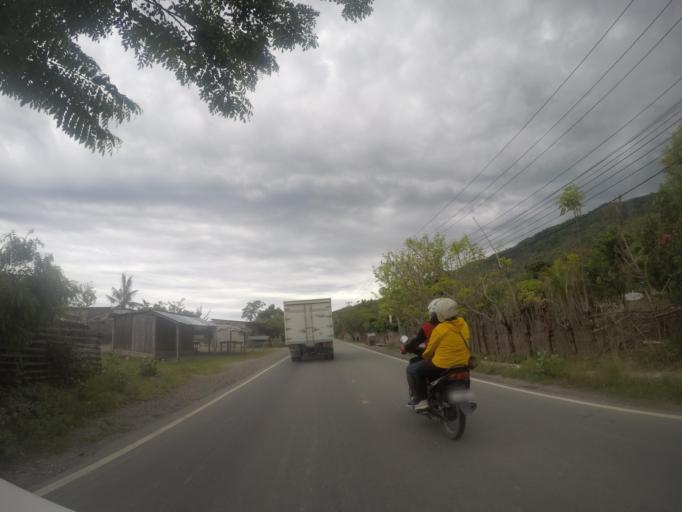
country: TL
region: Liquica
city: Liquica
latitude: -8.5800
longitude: 125.3610
